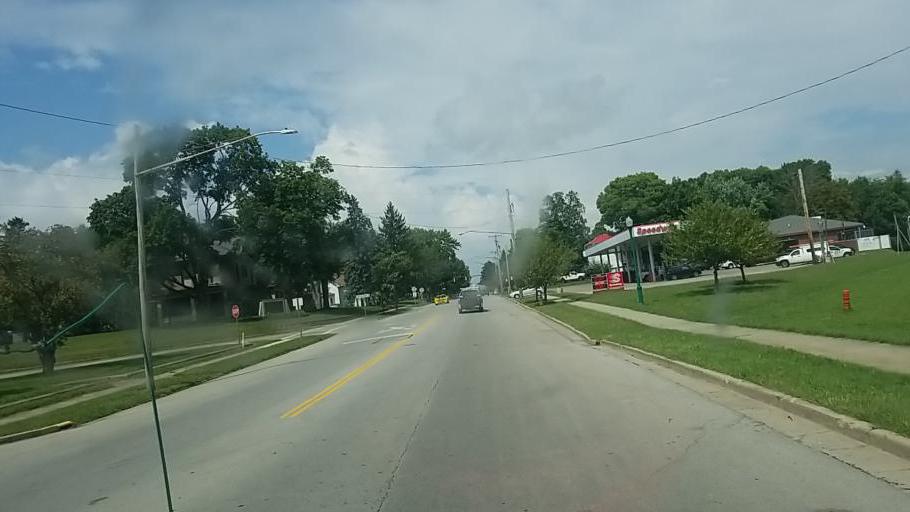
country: US
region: Ohio
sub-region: Champaign County
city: Urbana
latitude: 40.1153
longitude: -83.7513
